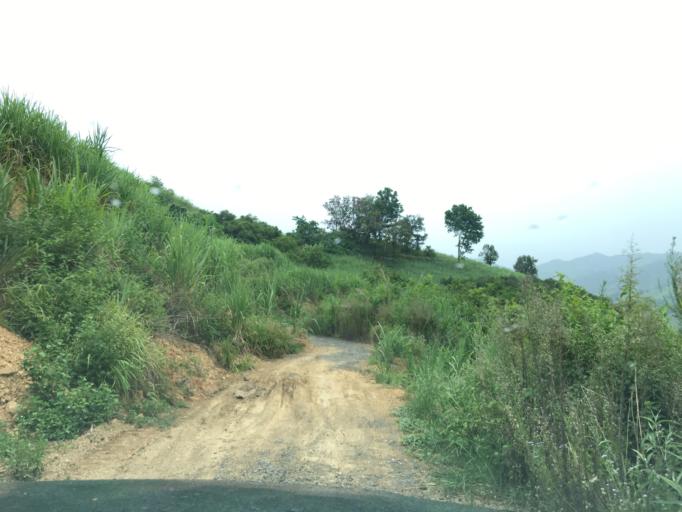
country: CN
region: Guangxi Zhuangzu Zizhiqu
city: Tongle
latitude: 25.0026
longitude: 105.9936
